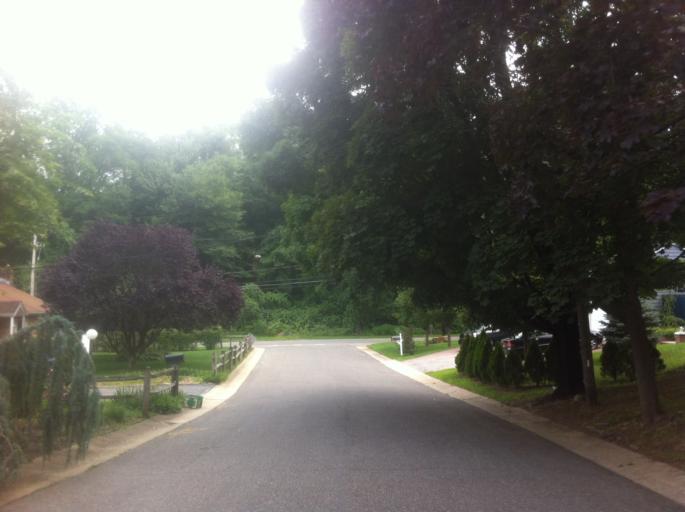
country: US
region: New York
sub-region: Nassau County
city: Oyster Bay
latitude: 40.8684
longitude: -73.5434
